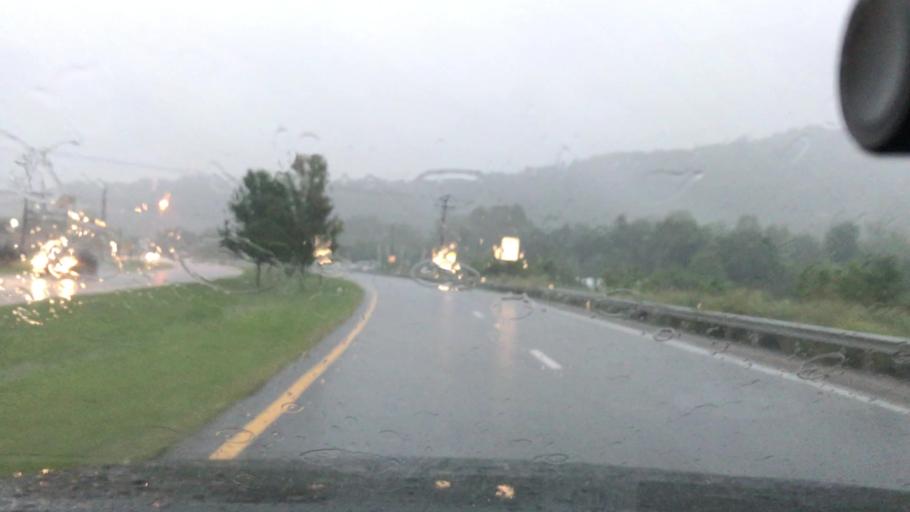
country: US
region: Virginia
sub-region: Giles County
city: Narrows
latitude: 37.3346
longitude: -80.8051
